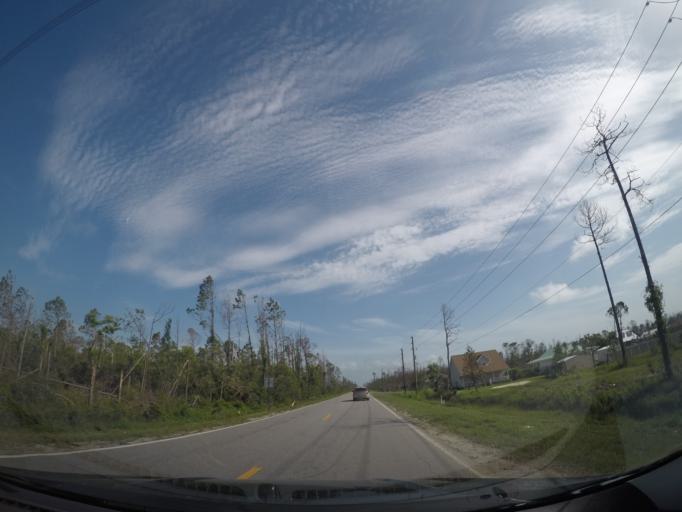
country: US
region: Florida
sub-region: Bay County
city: Mexico Beach
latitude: 29.9407
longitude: -85.3888
